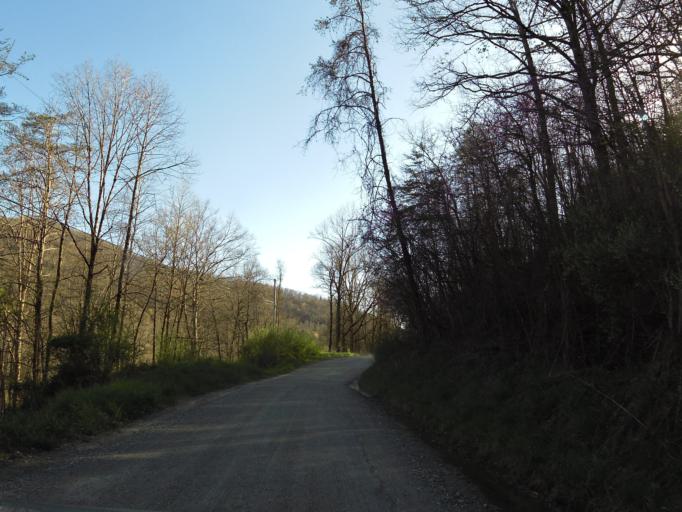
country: US
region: Tennessee
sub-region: Campbell County
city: Caryville
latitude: 36.2811
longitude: -84.3713
